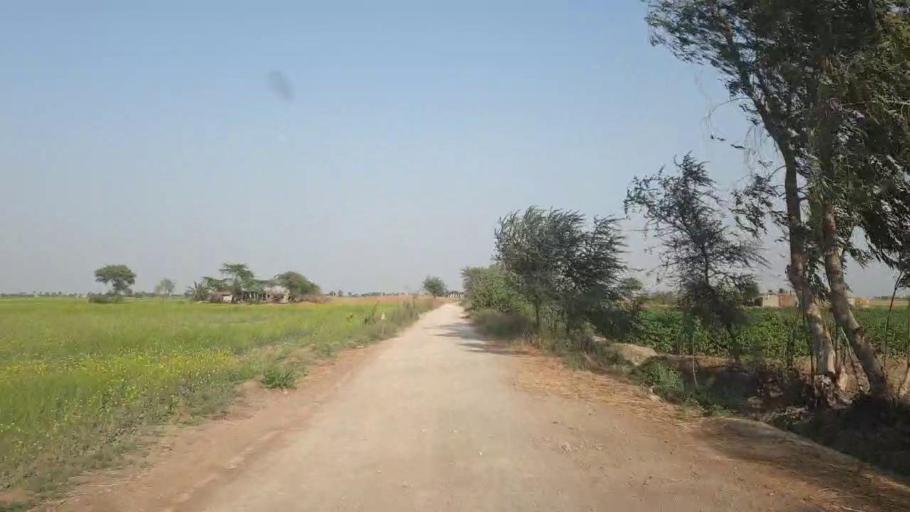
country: PK
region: Sindh
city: Kario
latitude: 24.5997
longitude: 68.5371
